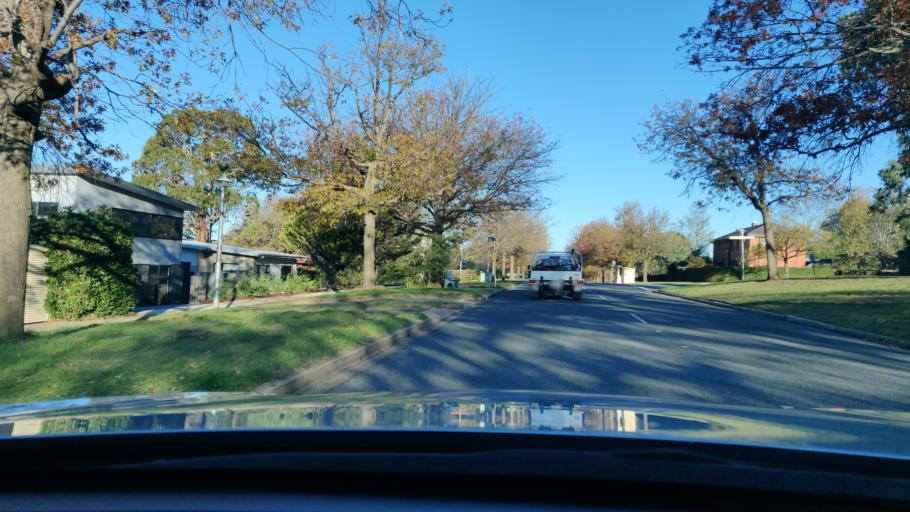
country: AU
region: Australian Capital Territory
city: Forrest
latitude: -35.3300
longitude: 149.1432
